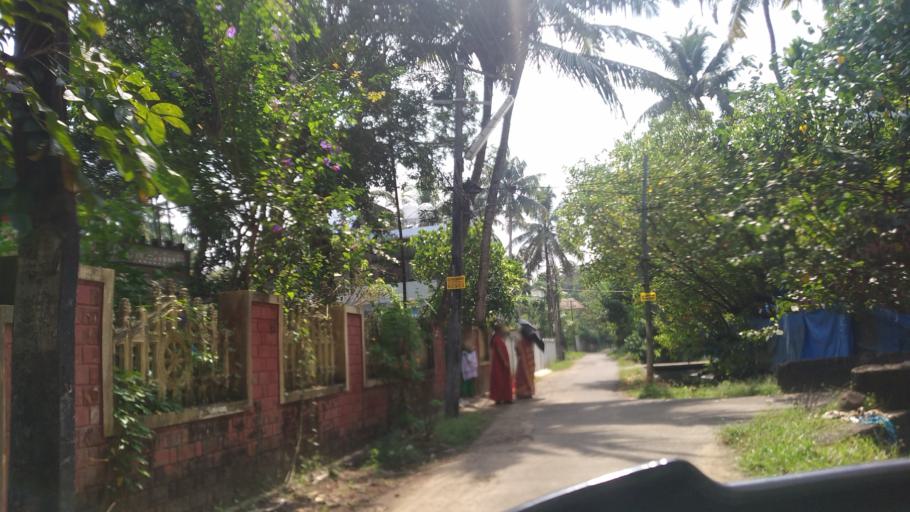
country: IN
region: Kerala
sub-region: Ernakulam
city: Elur
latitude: 10.0585
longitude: 76.2163
